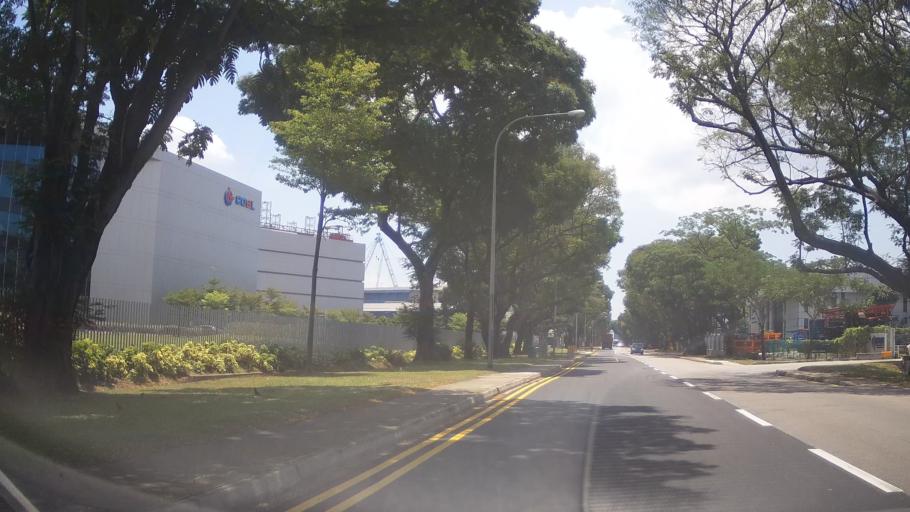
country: SG
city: Singapore
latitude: 1.3072
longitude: 103.6788
